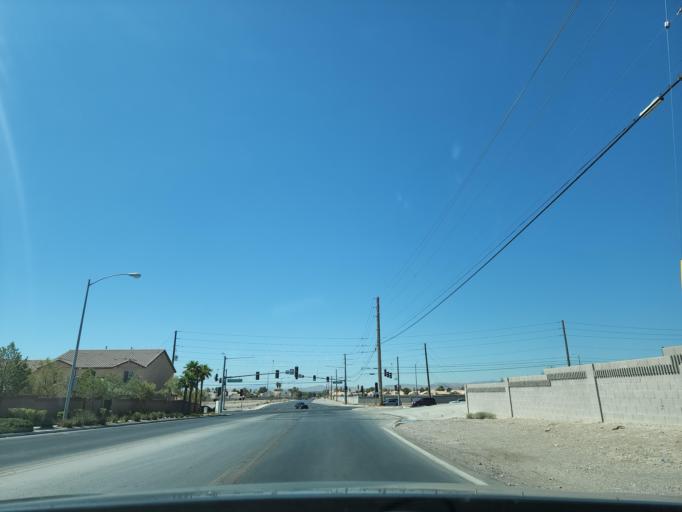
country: US
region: Nevada
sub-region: Clark County
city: Spring Valley
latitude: 36.1266
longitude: -115.2521
